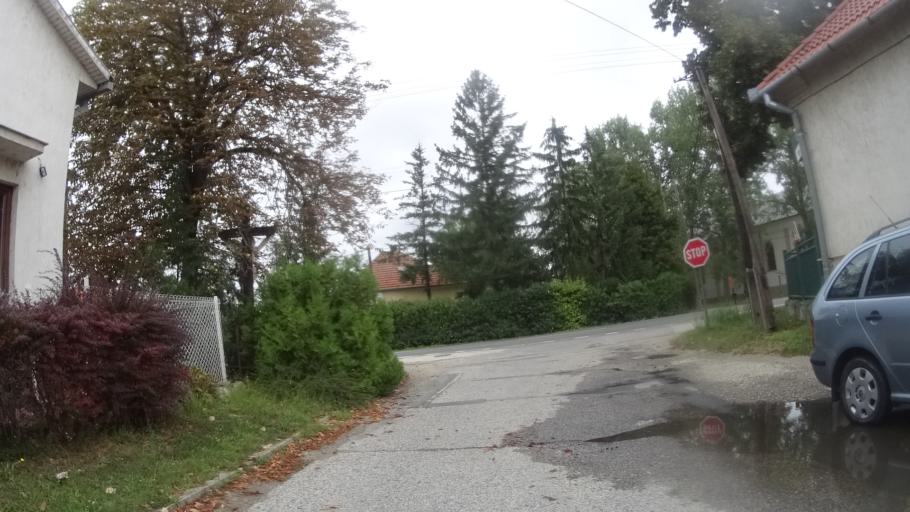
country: HU
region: Komarom-Esztergom
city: Acs
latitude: 47.7641
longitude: 18.0439
